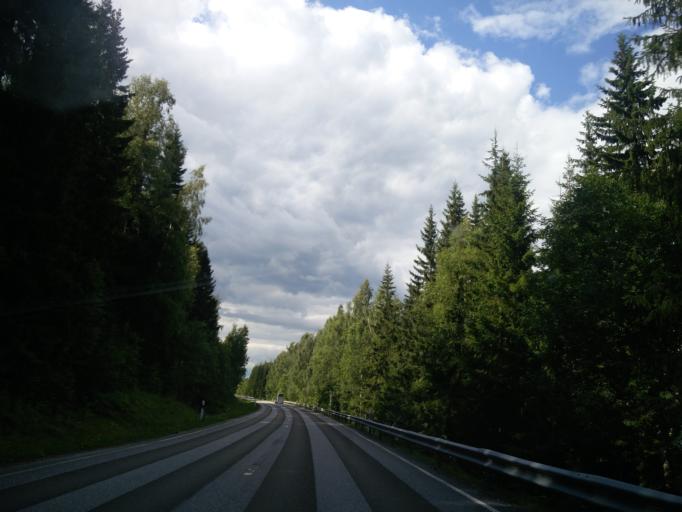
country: SE
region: OErebro
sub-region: Hallefors Kommun
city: Haellefors
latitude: 59.7569
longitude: 14.4356
